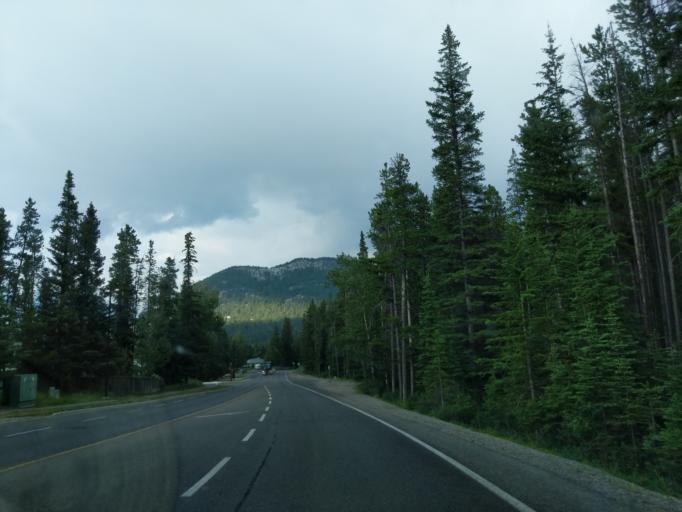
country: CA
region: Alberta
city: Banff
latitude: 51.1666
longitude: -115.5765
